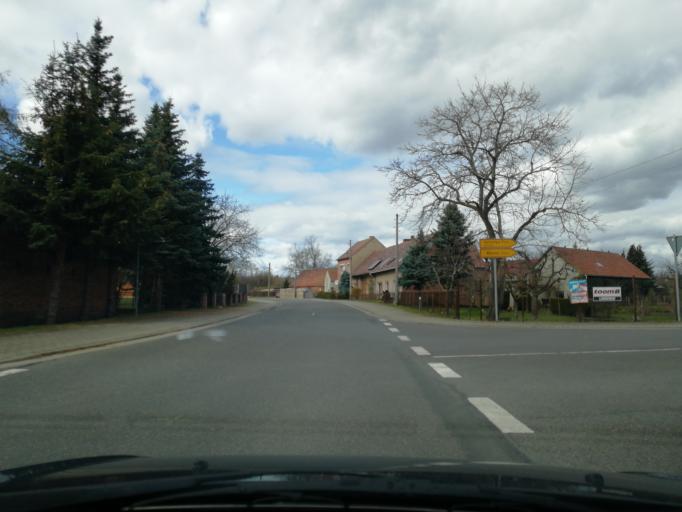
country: DE
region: Brandenburg
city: Altdobern
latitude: 51.7141
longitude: 14.0393
